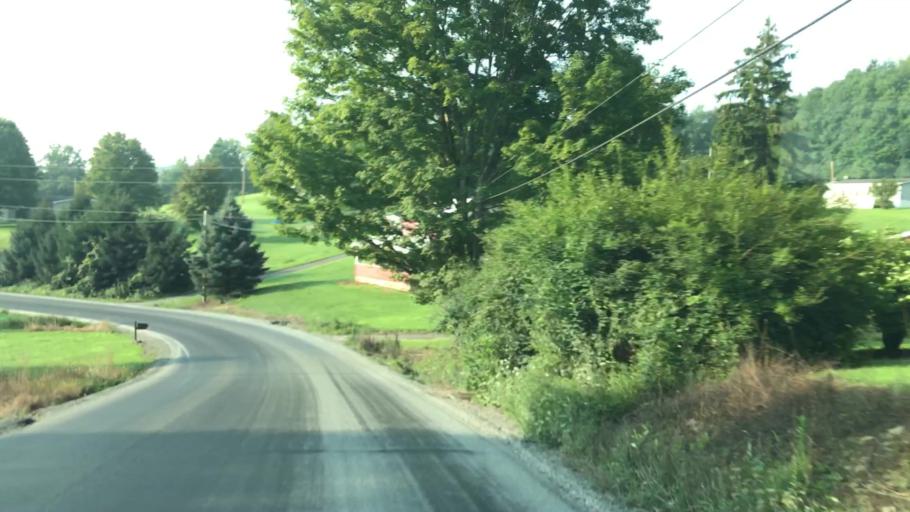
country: US
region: Pennsylvania
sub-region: Wyoming County
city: Factoryville
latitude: 41.6592
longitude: -75.8026
